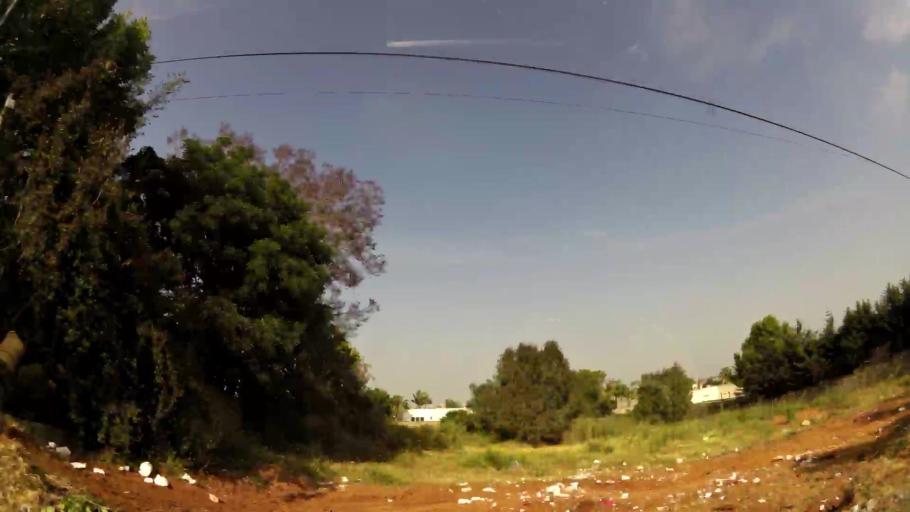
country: MA
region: Rabat-Sale-Zemmour-Zaer
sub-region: Rabat
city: Rabat
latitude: 33.9361
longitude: -6.8052
